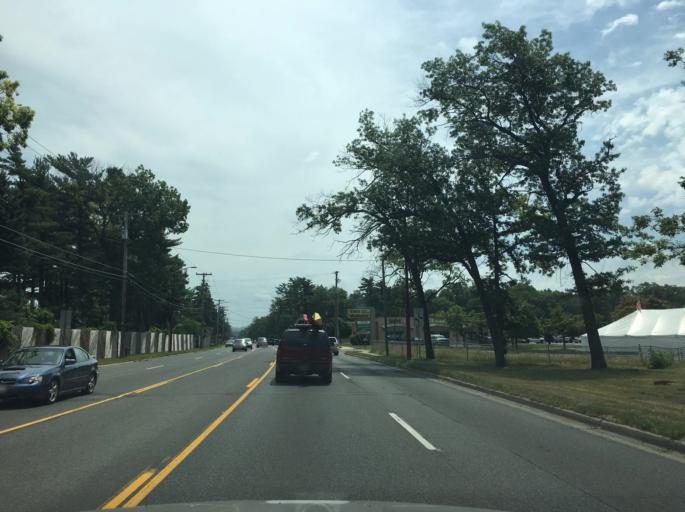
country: US
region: Michigan
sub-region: Grand Traverse County
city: Traverse City
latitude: 44.7555
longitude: -85.5738
